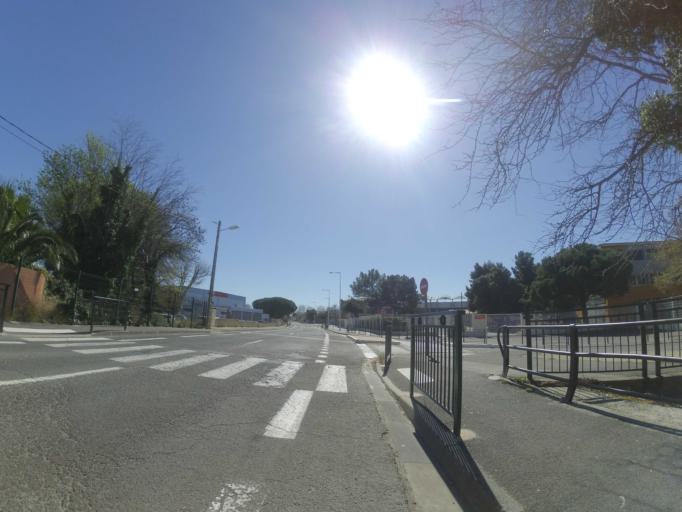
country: FR
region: Languedoc-Roussillon
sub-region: Departement des Pyrenees-Orientales
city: Perpignan
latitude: 42.7175
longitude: 2.8908
